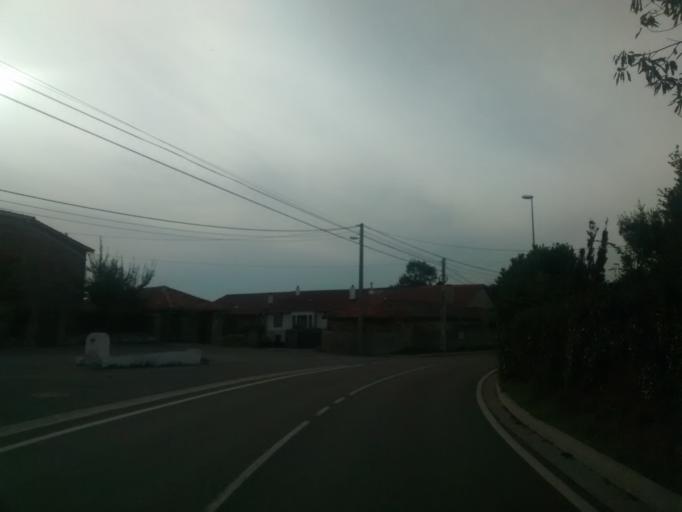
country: ES
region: Castille and Leon
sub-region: Provincia de Burgos
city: Arija
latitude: 42.9875
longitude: -3.9842
